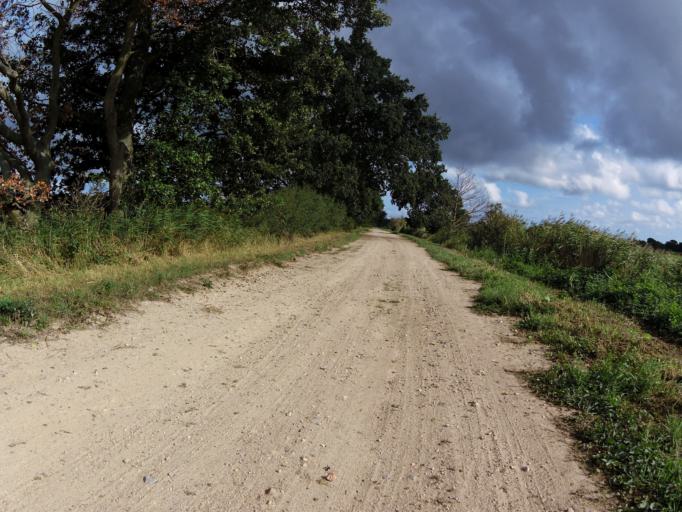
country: DE
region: Mecklenburg-Vorpommern
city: Loddin
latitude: 53.9863
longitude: 14.0597
